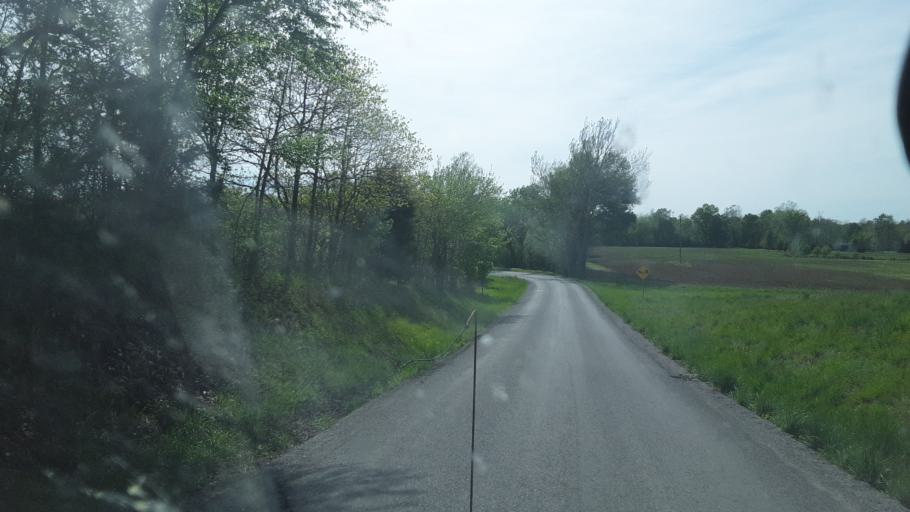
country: US
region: Illinois
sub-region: Jackson County
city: Carbondale
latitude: 37.6809
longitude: -89.2935
